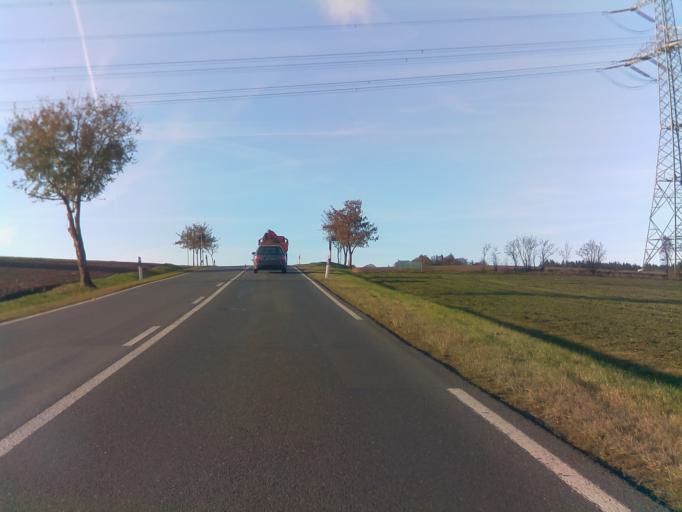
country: DE
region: Thuringia
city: Wittgendorf
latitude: 50.5948
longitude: 11.3012
